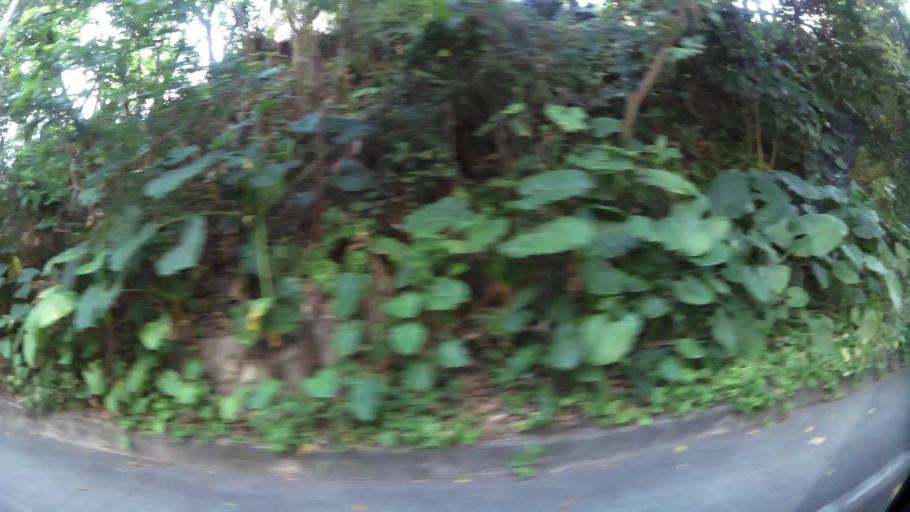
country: HK
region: Wanchai
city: Wan Chai
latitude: 22.2701
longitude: 114.1914
